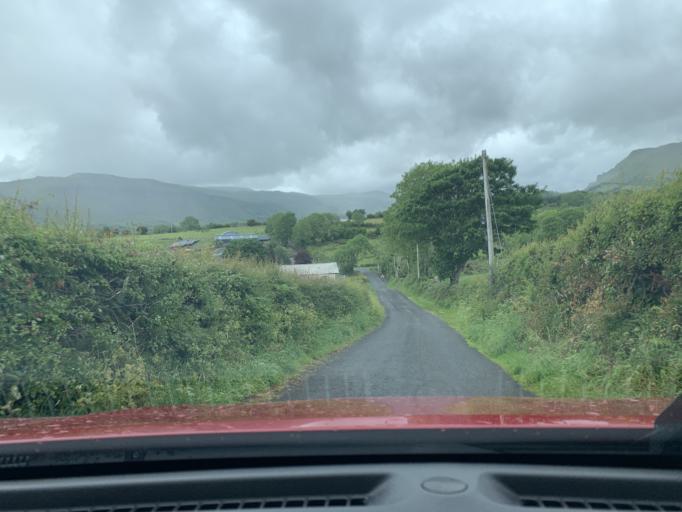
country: IE
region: Connaught
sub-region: Sligo
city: Sligo
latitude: 54.3096
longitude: -8.4546
